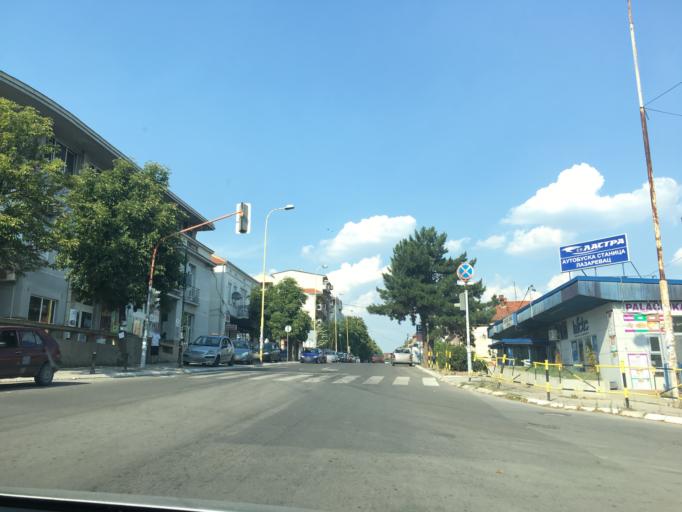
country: RS
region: Central Serbia
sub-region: Belgrade
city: Lazarevac
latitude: 44.3793
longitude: 20.2638
